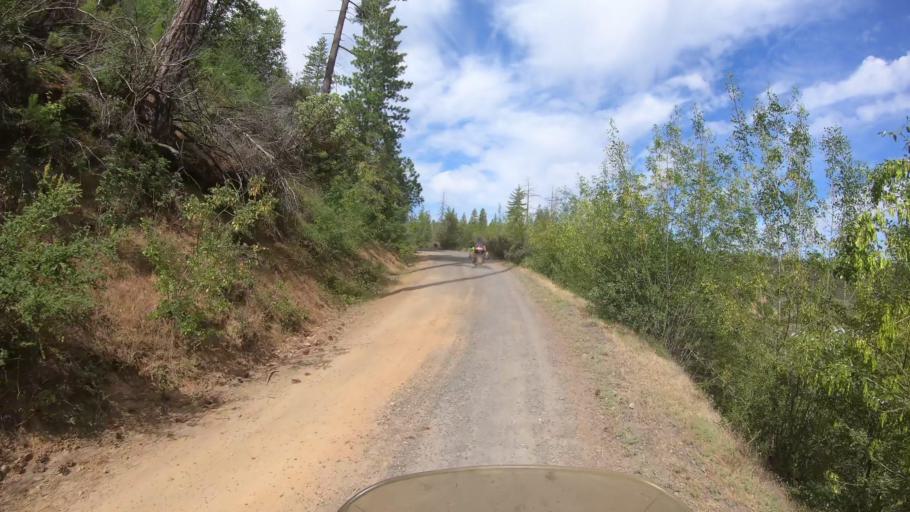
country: US
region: California
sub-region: Tuolumne County
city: Tuolumne City
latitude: 37.8323
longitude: -120.1135
